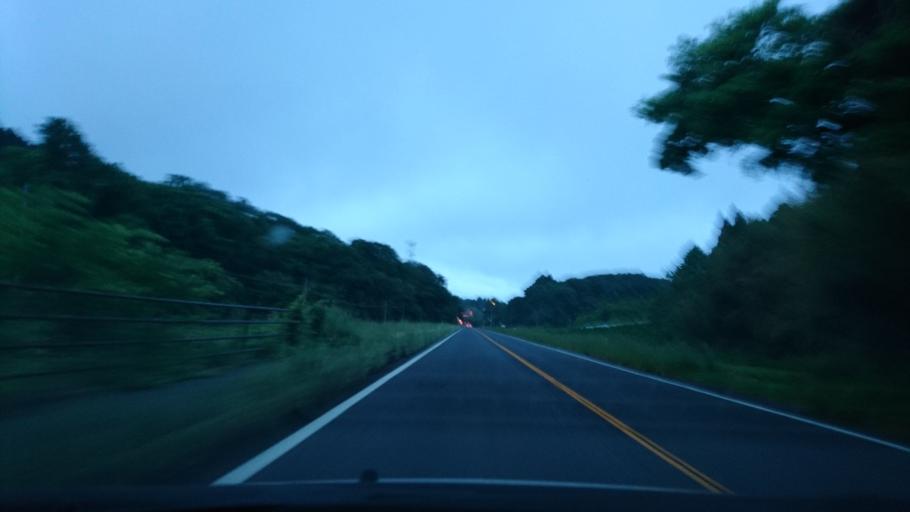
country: JP
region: Iwate
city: Ichinoseki
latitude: 38.8618
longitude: 141.1049
